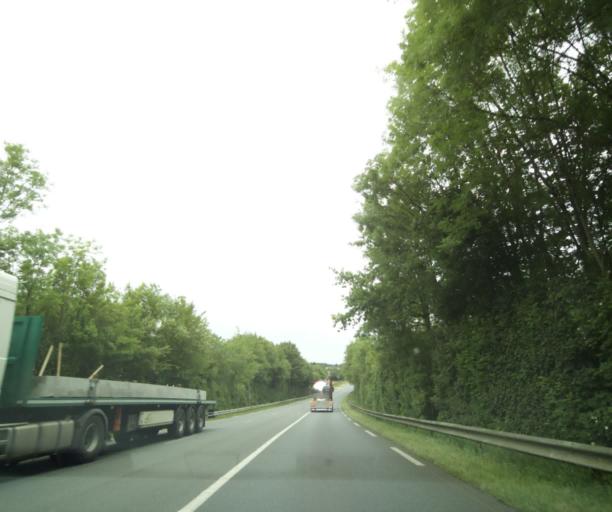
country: FR
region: Poitou-Charentes
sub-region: Departement des Deux-Sevres
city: Champdeniers-Saint-Denis
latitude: 46.4802
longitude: -0.3596
